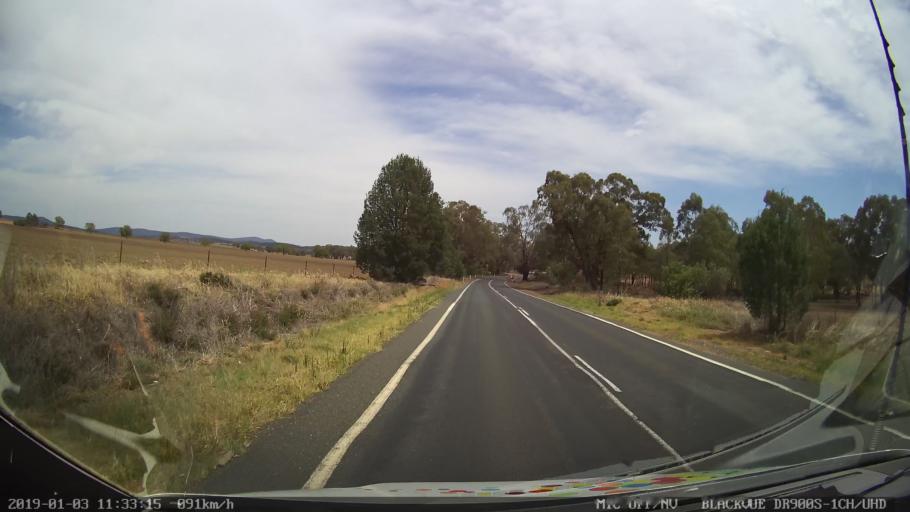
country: AU
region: New South Wales
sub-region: Weddin
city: Grenfell
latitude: -33.9490
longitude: 148.1725
